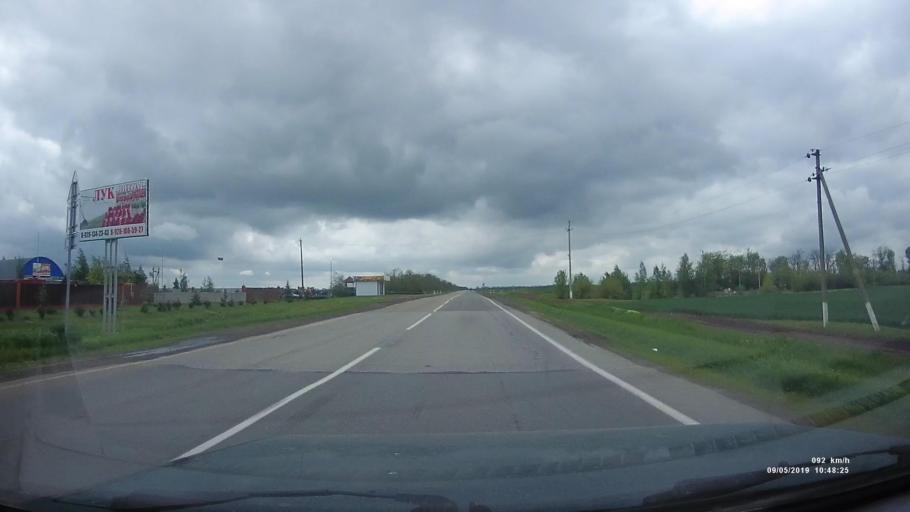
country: RU
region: Rostov
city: Peshkovo
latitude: 46.9568
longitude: 39.3557
